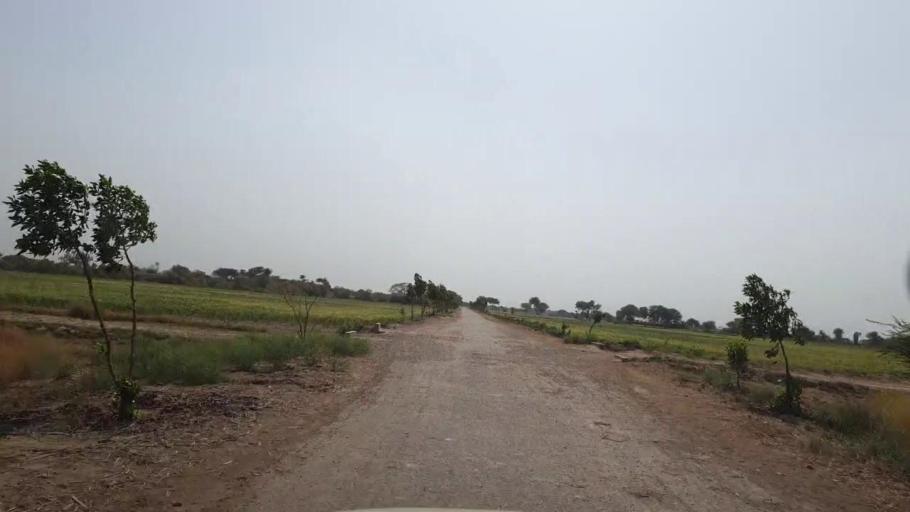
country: PK
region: Sindh
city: Matli
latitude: 25.0444
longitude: 68.6854
